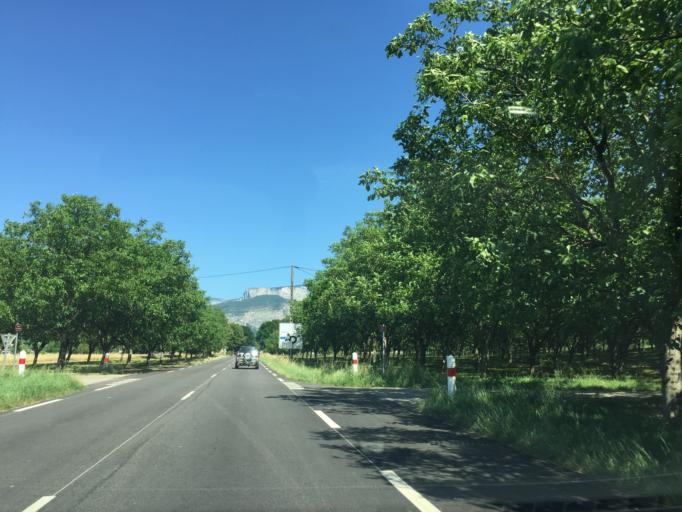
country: FR
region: Rhone-Alpes
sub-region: Departement de l'Isere
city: Saint-Just-de-Claix
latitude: 45.0551
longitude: 5.2815
